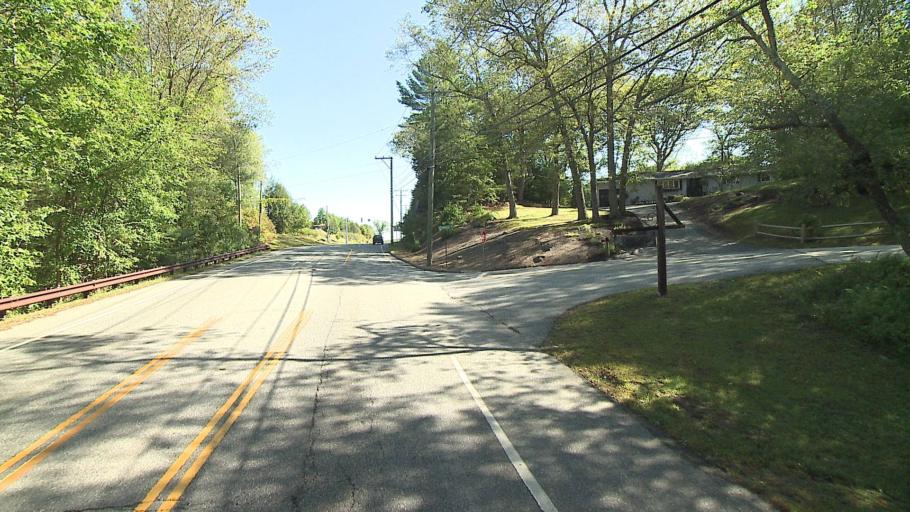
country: US
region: Connecticut
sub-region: New London County
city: Lisbon
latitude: 41.5830
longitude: -71.9966
